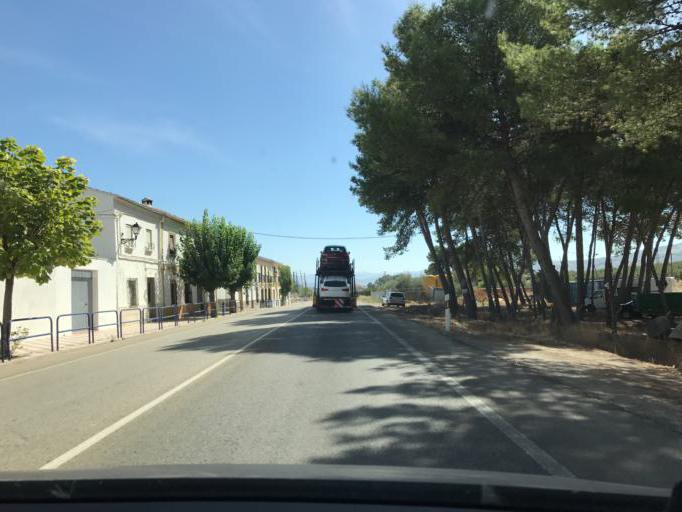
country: ES
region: Andalusia
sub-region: Province of Cordoba
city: Luque
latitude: 37.5732
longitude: -4.2619
